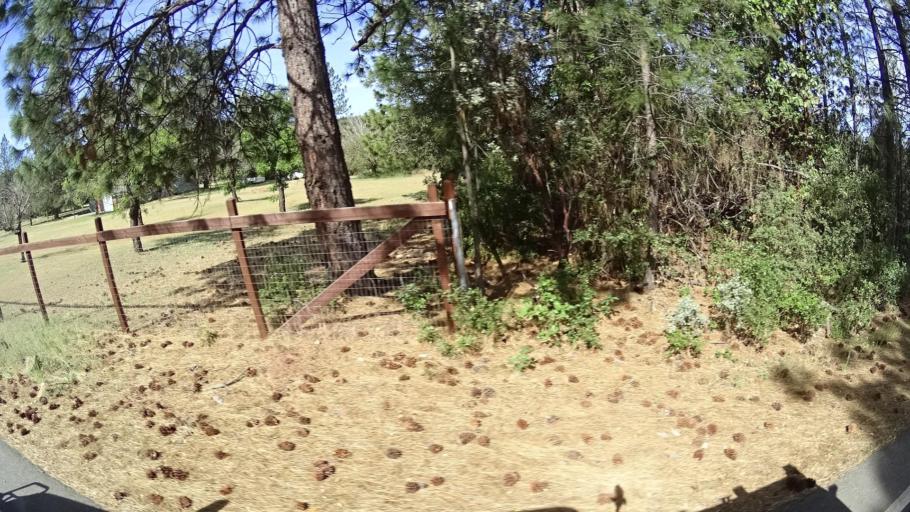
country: US
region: California
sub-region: Lake County
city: Soda Bay
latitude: 38.9098
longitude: -122.7657
